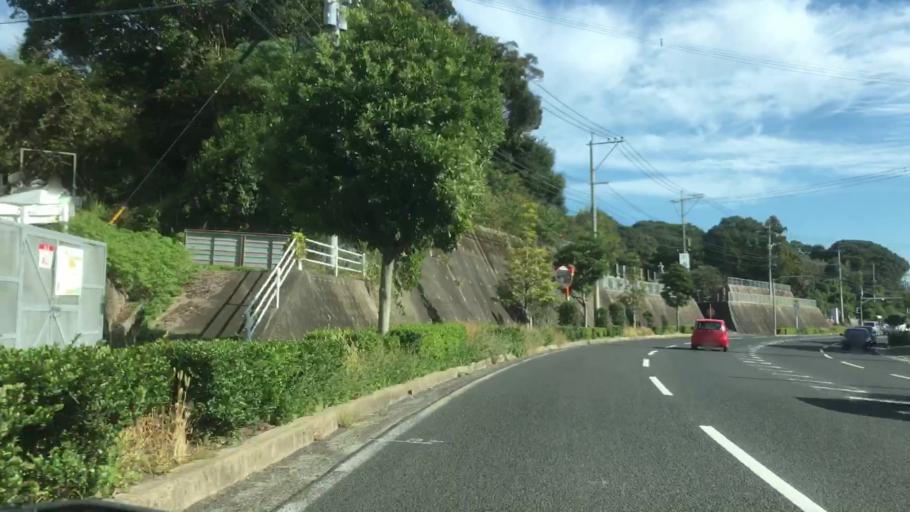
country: JP
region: Nagasaki
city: Sasebo
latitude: 33.1130
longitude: 129.7876
